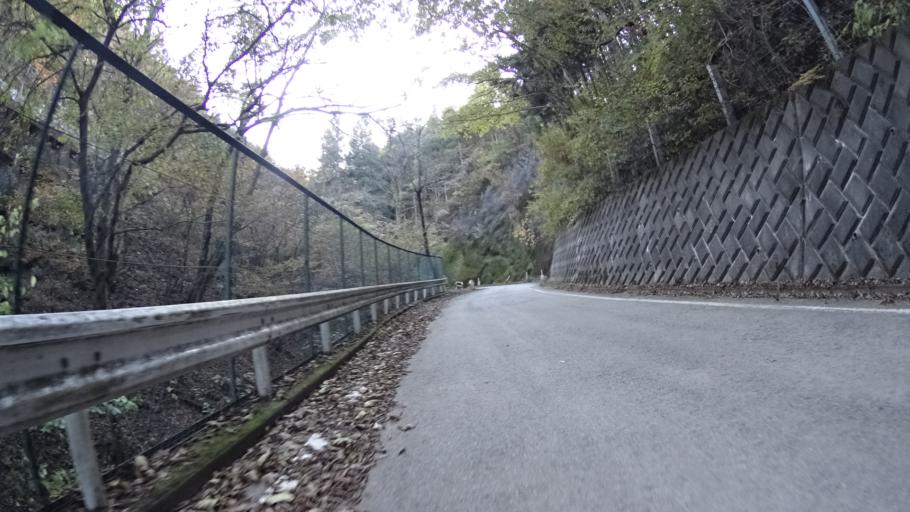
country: JP
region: Yamanashi
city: Uenohara
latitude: 35.6577
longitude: 139.1674
